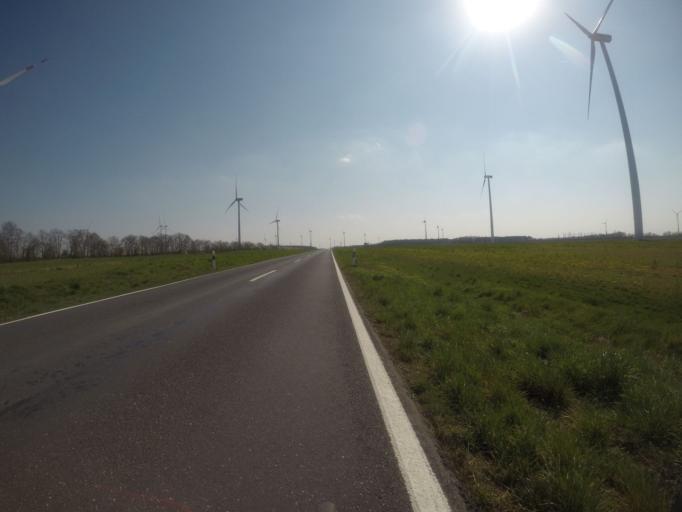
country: DE
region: Brandenburg
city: Nauen
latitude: 52.5497
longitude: 12.8713
